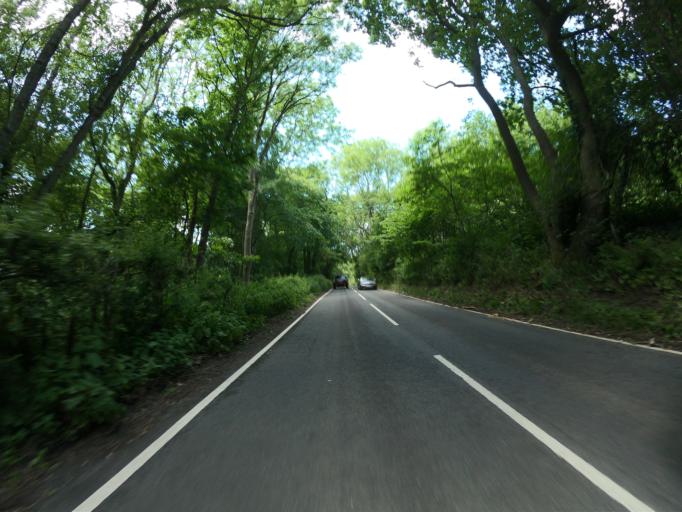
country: GB
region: England
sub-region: Kent
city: Halstead
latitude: 51.3080
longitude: 0.1394
